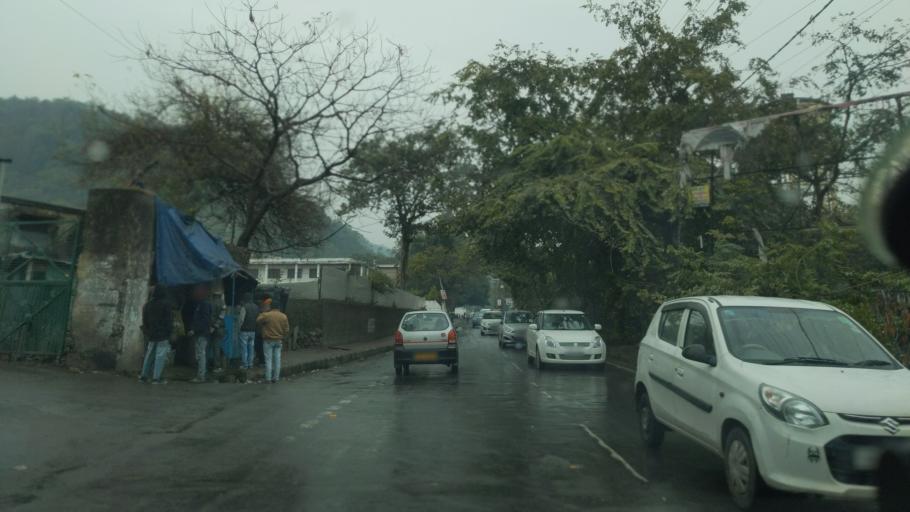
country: IN
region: Uttarakhand
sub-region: Naini Tal
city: Haldwani
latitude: 29.2675
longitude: 79.5445
